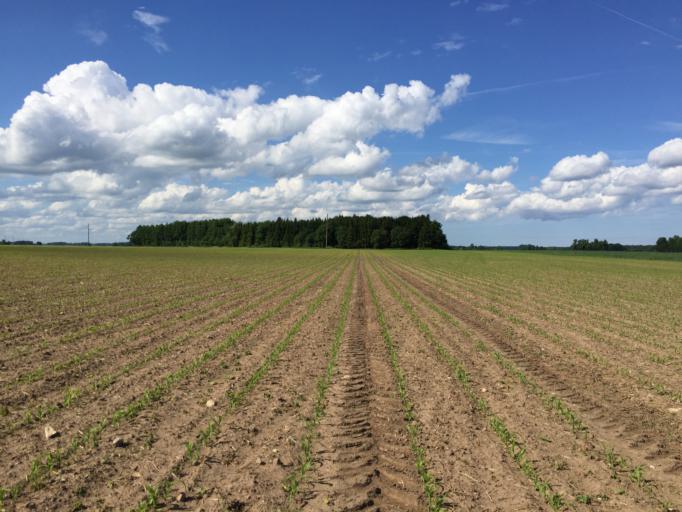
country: LV
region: Dobeles Rajons
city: Dobele
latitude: 56.6782
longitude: 23.3986
